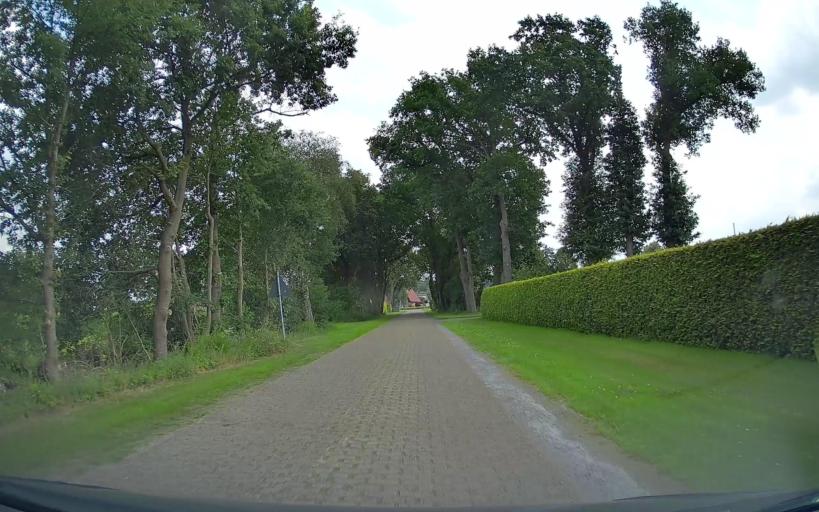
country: DE
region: Lower Saxony
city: Bosel
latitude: 53.0170
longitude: 7.9478
